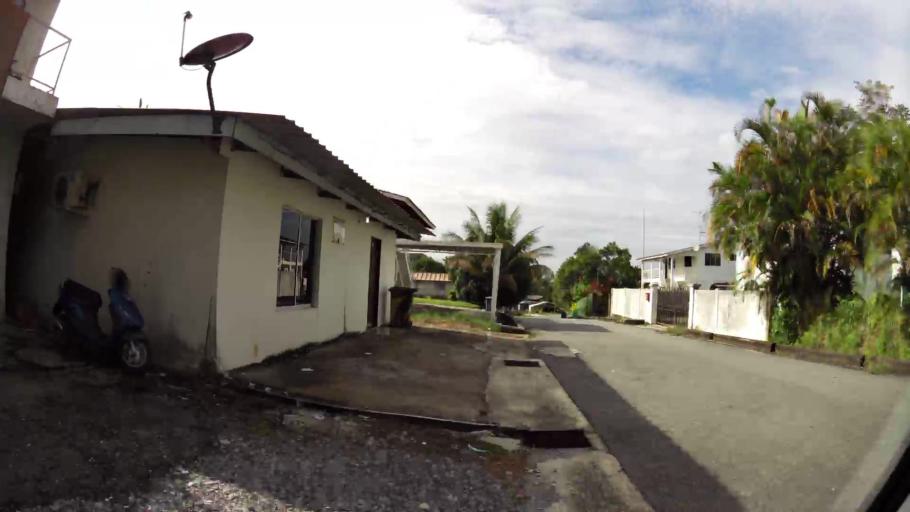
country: BN
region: Brunei and Muara
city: Bandar Seri Begawan
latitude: 4.9004
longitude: 114.8892
